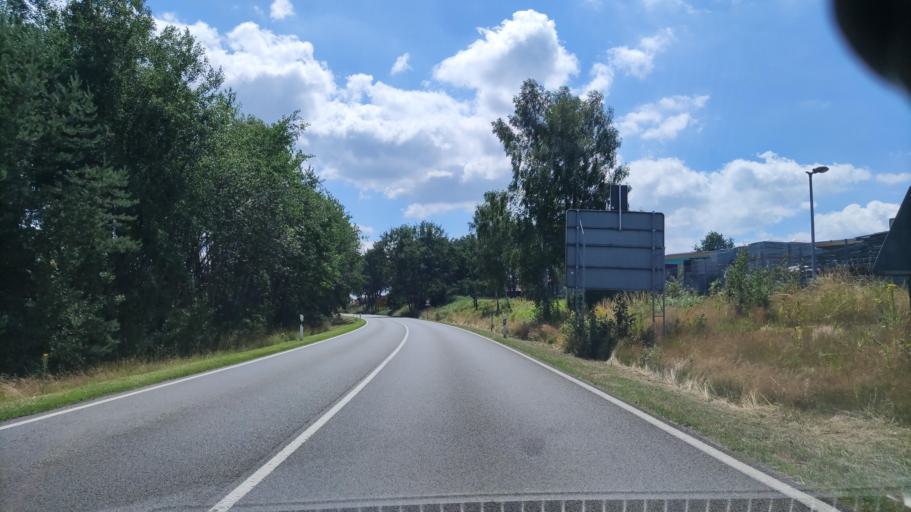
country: DE
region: Mecklenburg-Vorpommern
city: Wittenburg
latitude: 53.5018
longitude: 11.0961
